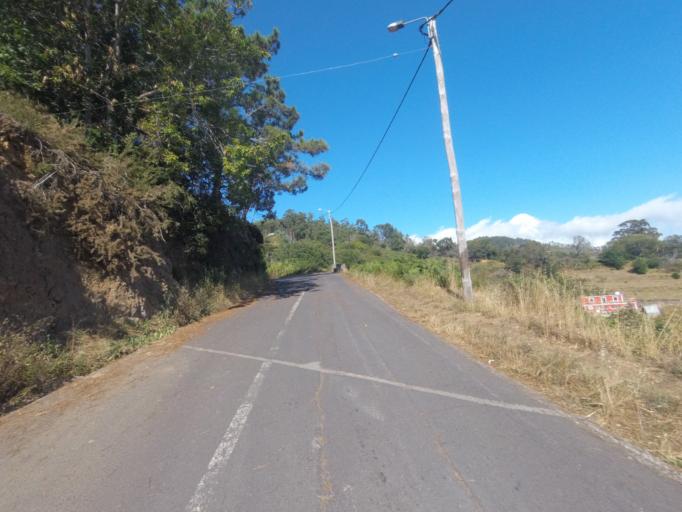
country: PT
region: Madeira
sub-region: Ribeira Brava
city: Campanario
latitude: 32.6977
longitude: -17.0187
